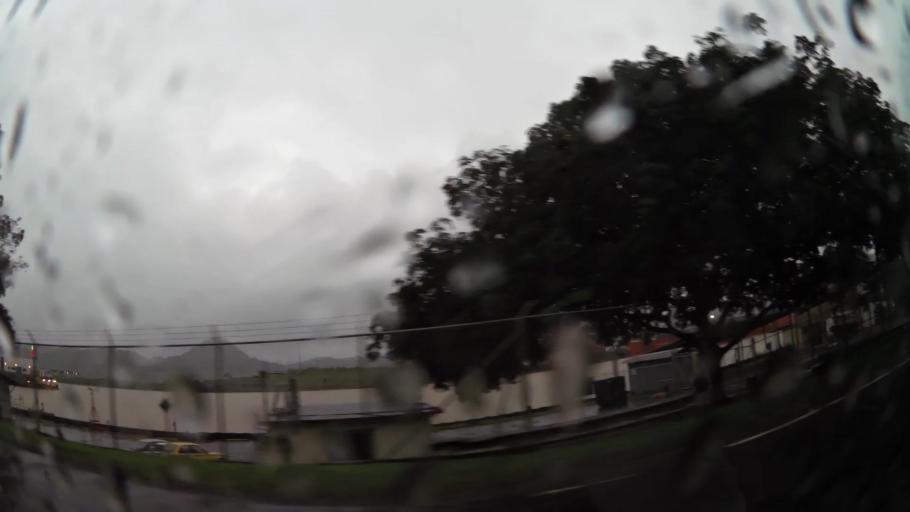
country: PA
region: Panama
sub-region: Distrito de Panama
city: Paraiso
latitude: 9.0230
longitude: -79.6174
